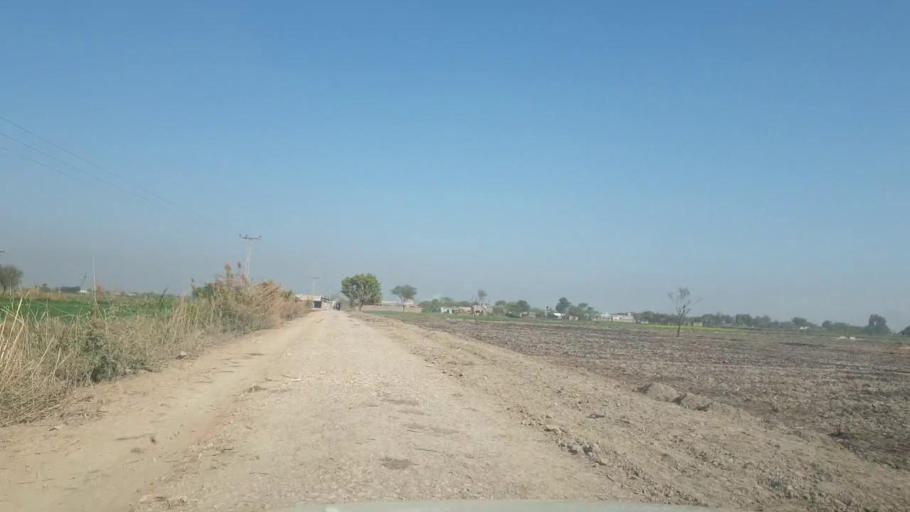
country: PK
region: Sindh
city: Mirpur Khas
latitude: 25.5024
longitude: 69.1548
